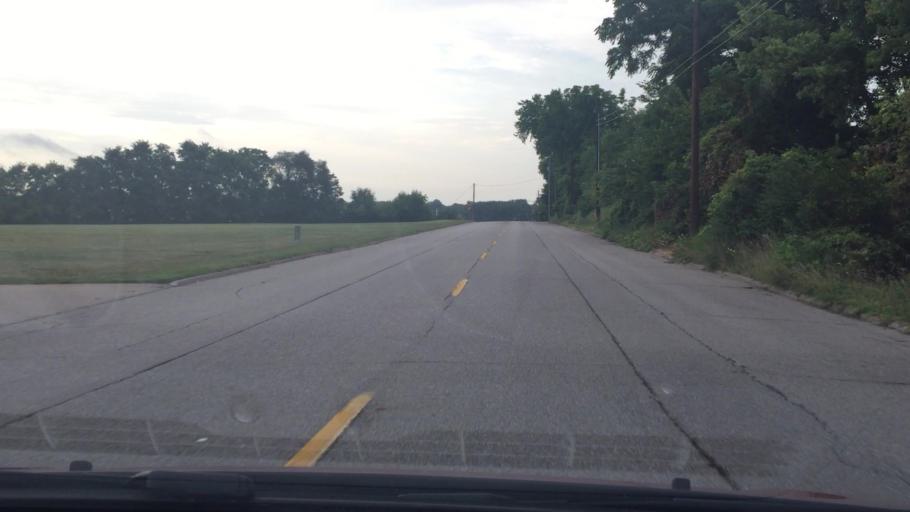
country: US
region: Iowa
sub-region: Muscatine County
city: Muscatine
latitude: 41.4404
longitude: -91.0463
